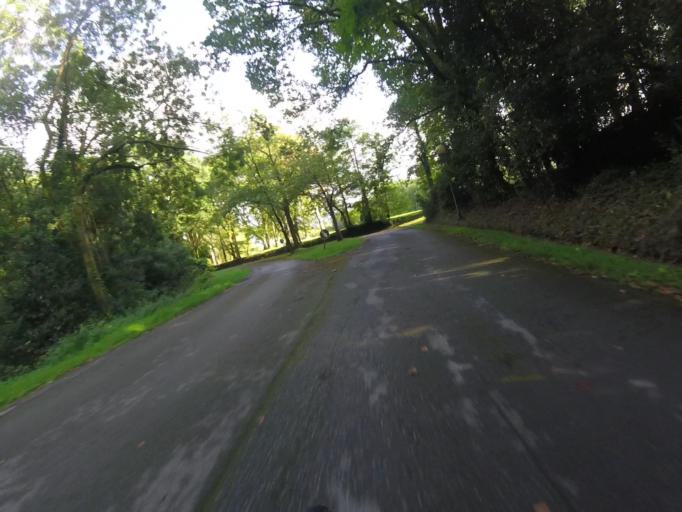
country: ES
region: Basque Country
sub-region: Provincia de Guipuzcoa
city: Irun
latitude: 43.3417
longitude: -1.8321
